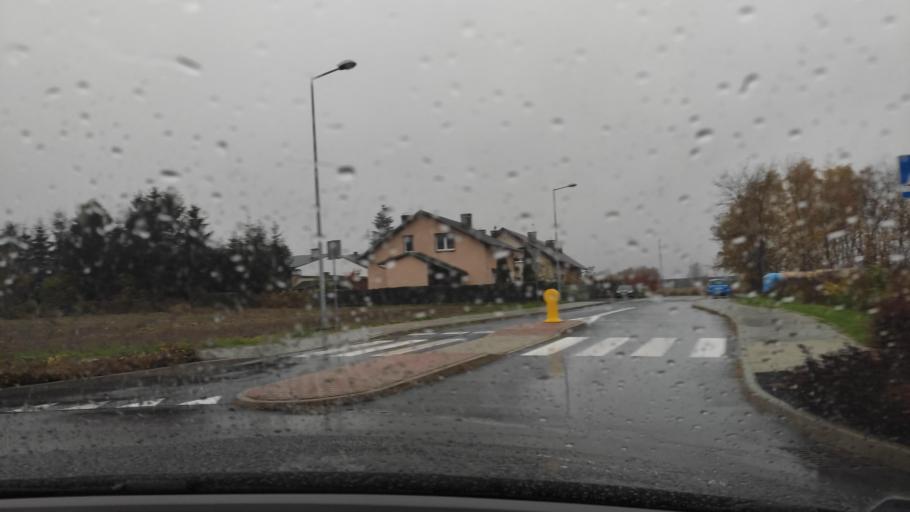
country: PL
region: Greater Poland Voivodeship
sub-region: Powiat poznanski
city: Kornik
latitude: 52.2546
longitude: 17.0866
